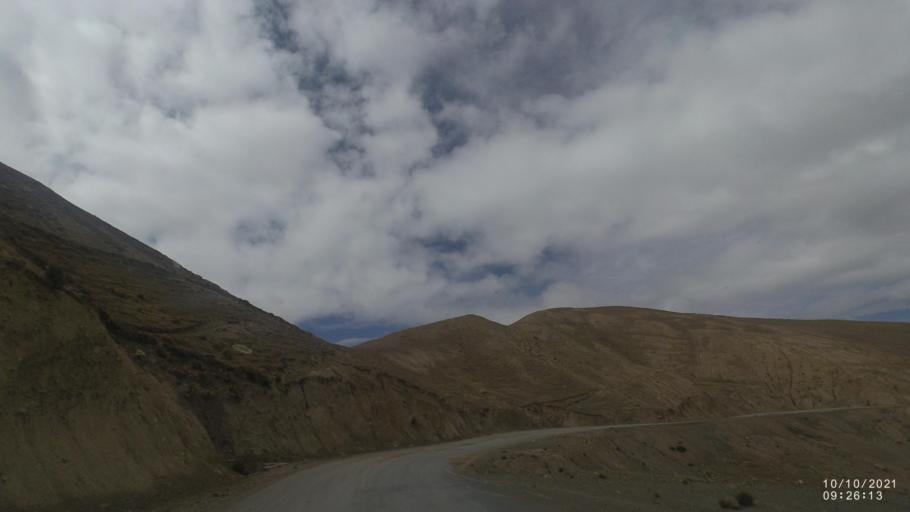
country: BO
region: La Paz
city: Quime
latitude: -17.0949
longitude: -67.3195
